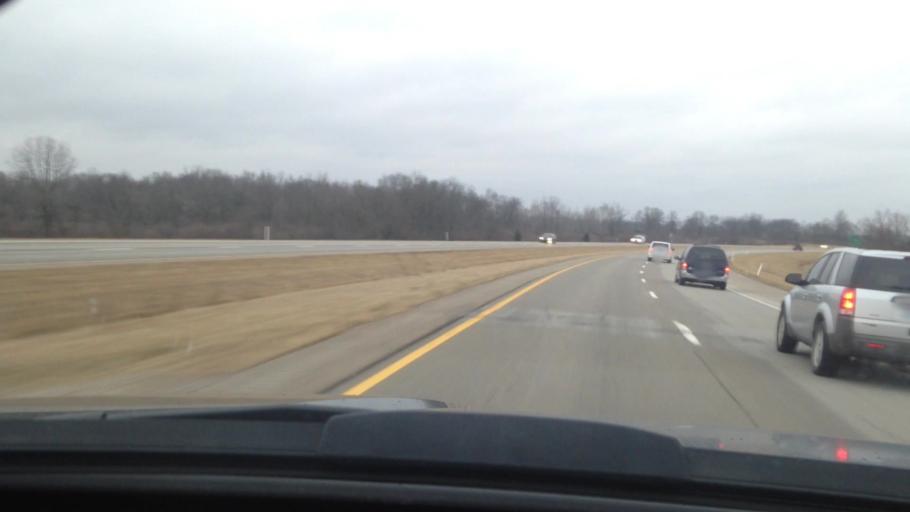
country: US
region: Indiana
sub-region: Delaware County
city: Muncie
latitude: 40.1580
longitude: -85.3534
